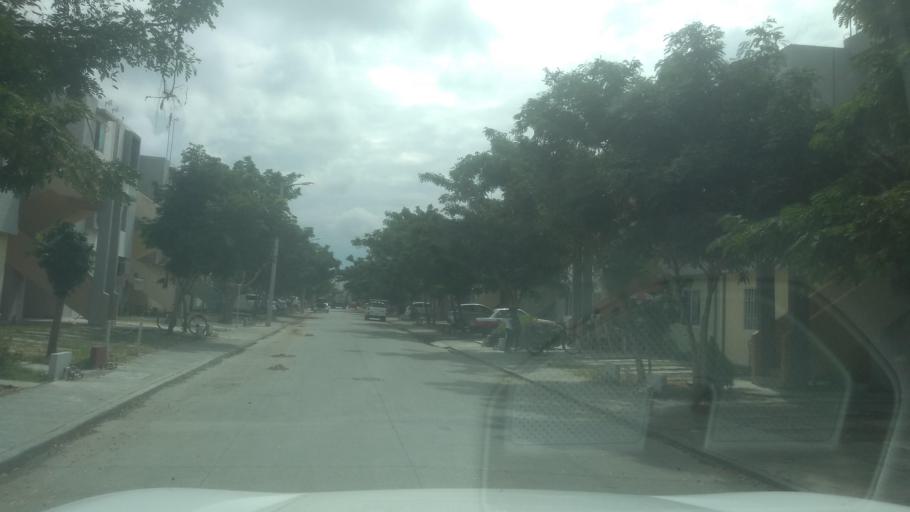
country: MX
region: Veracruz
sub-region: Medellin
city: Fraccionamiento Arboledas San Ramon
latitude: 19.0929
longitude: -96.1683
